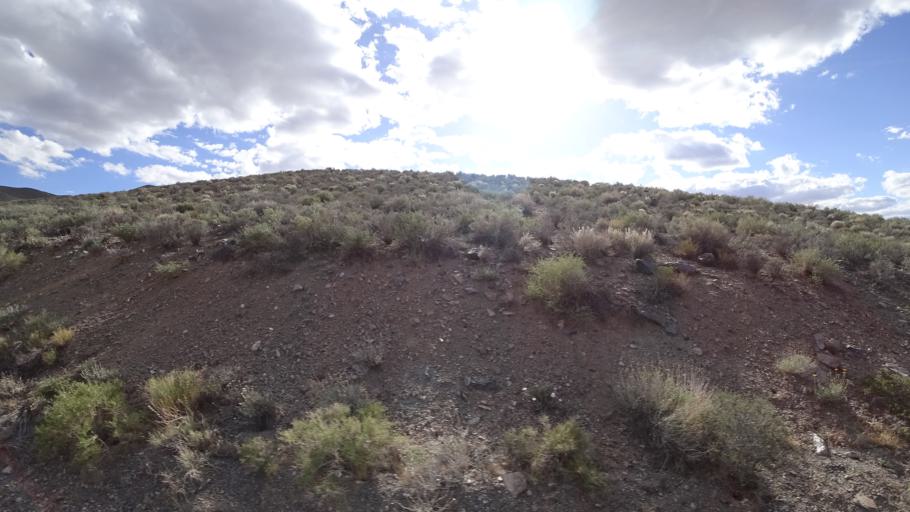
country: US
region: Nevada
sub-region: Nye County
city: Beatty
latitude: 36.3999
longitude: -117.1667
